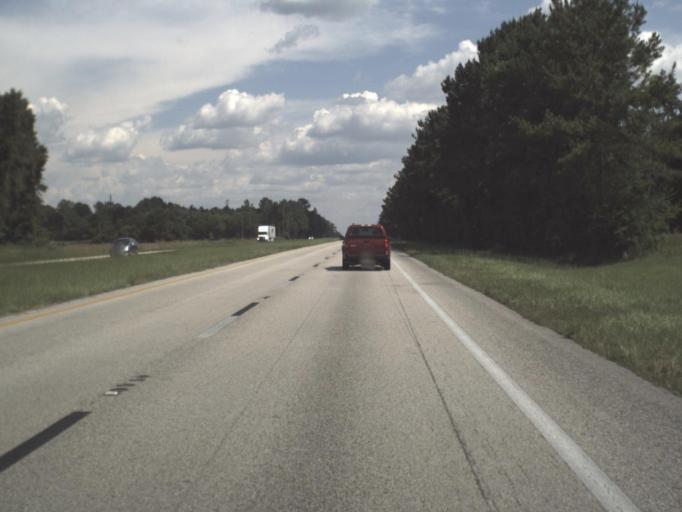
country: US
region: Florida
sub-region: Alachua County
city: Hawthorne
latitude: 29.6739
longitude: -82.1212
